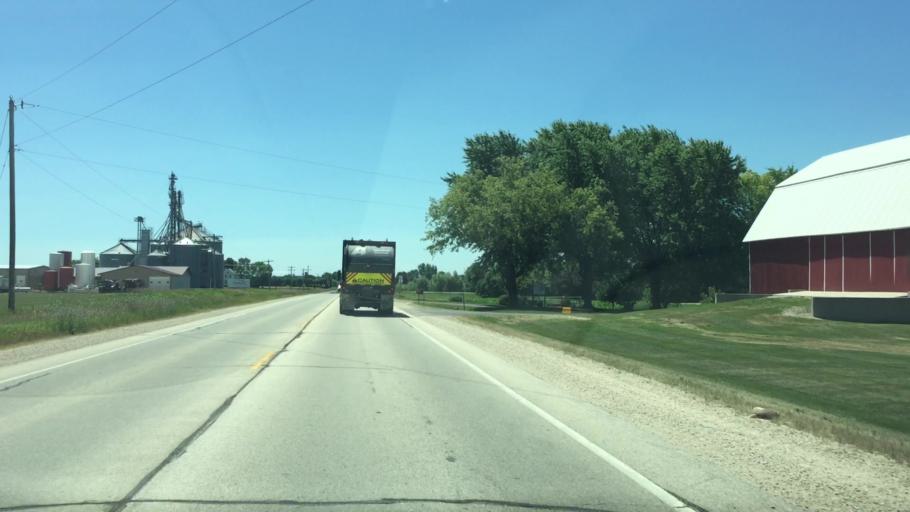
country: US
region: Wisconsin
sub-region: Calumet County
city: Chilton
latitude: 44.0769
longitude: -88.1634
